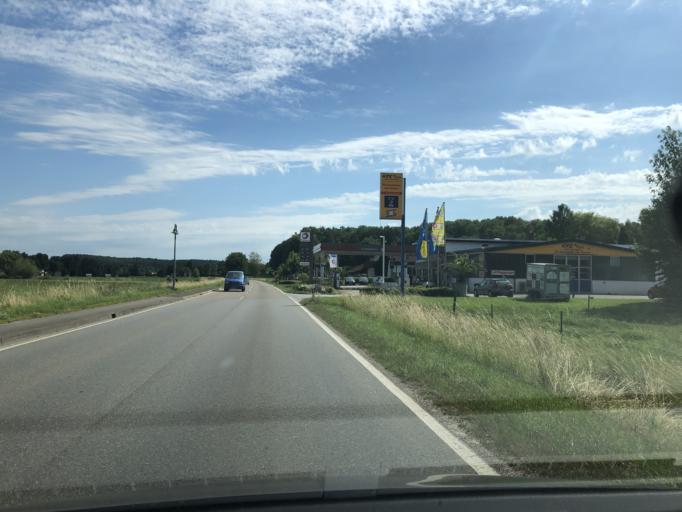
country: DE
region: Baden-Wuerttemberg
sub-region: Karlsruhe Region
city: Aglasterhausen
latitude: 49.3673
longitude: 8.9817
